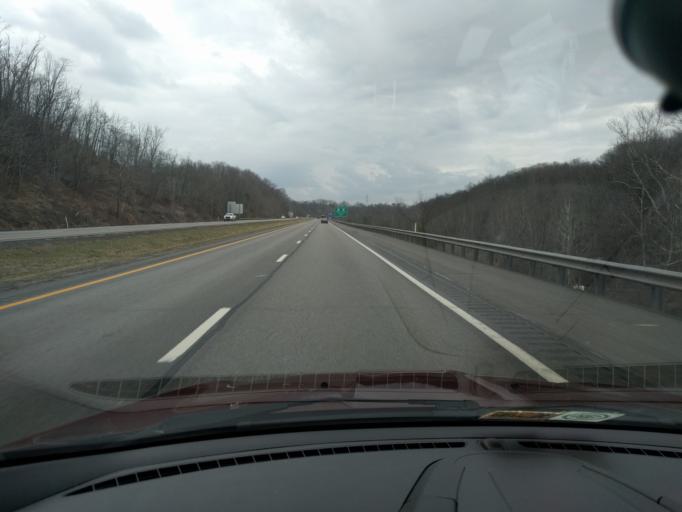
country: US
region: West Virginia
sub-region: Wood County
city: Vienna
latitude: 39.2969
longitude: -81.4920
